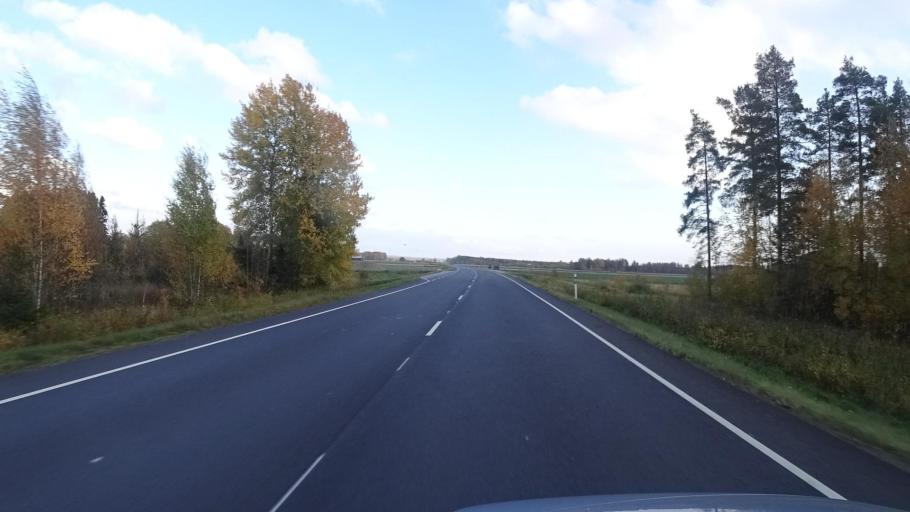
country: FI
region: Satakunta
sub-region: Rauma
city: Koeylioe
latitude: 61.0785
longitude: 22.2812
